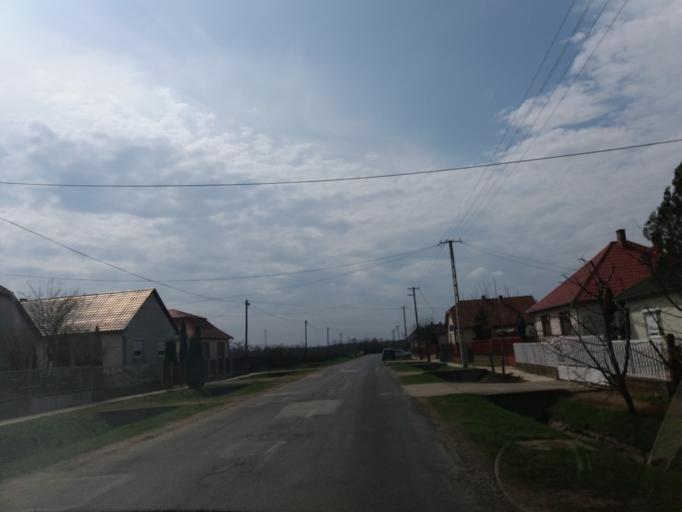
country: HU
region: Szabolcs-Szatmar-Bereg
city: Petnehaza
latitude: 48.0598
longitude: 22.0705
